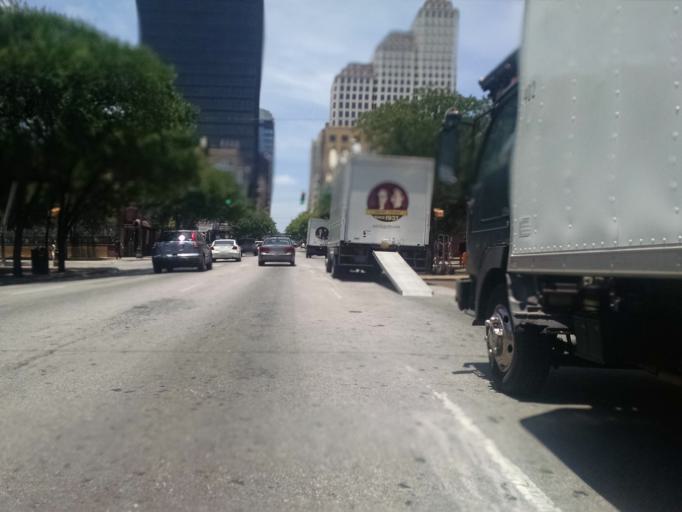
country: US
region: Texas
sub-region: Travis County
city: Austin
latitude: 30.2673
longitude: -97.7400
